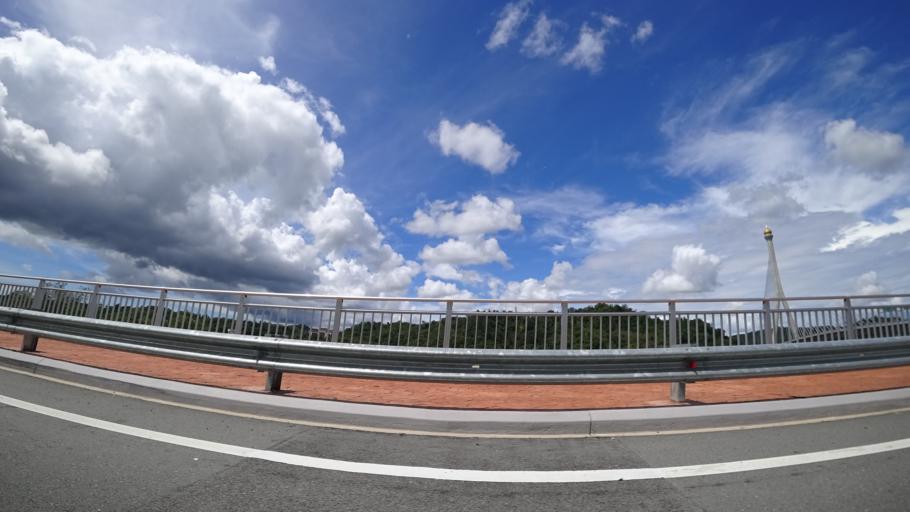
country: BN
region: Brunei and Muara
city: Bandar Seri Begawan
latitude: 4.8783
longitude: 114.9456
